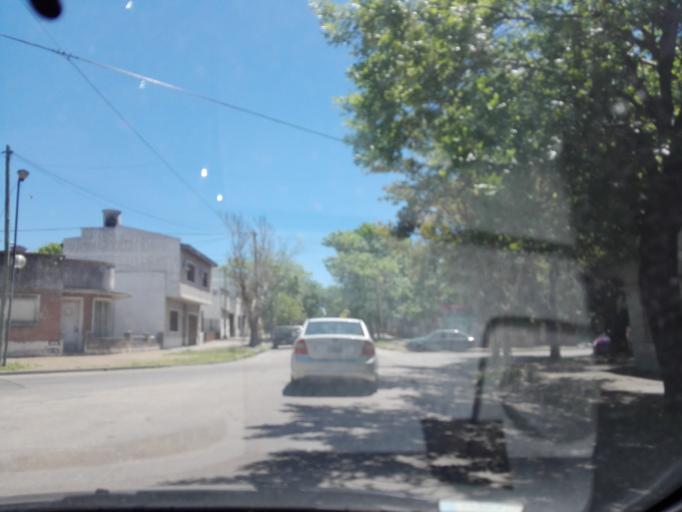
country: AR
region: Buenos Aires
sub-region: Partido de La Plata
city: La Plata
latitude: -34.9285
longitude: -57.9678
